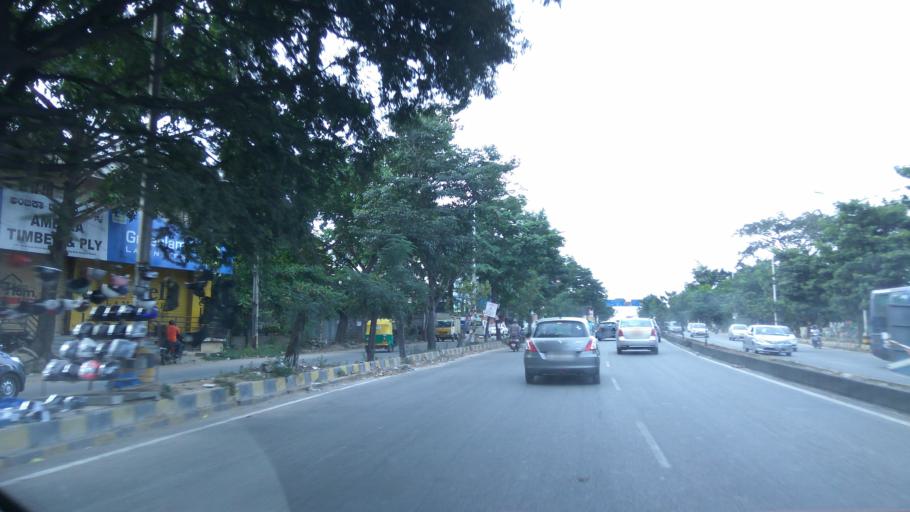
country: IN
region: Karnataka
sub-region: Bangalore Urban
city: Bangalore
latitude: 13.0080
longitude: 77.6626
